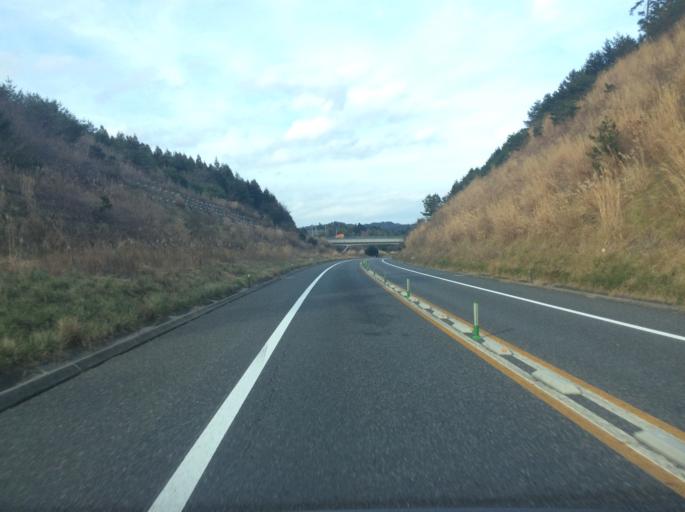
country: JP
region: Fukushima
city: Iwaki
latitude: 37.2213
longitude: 140.9763
